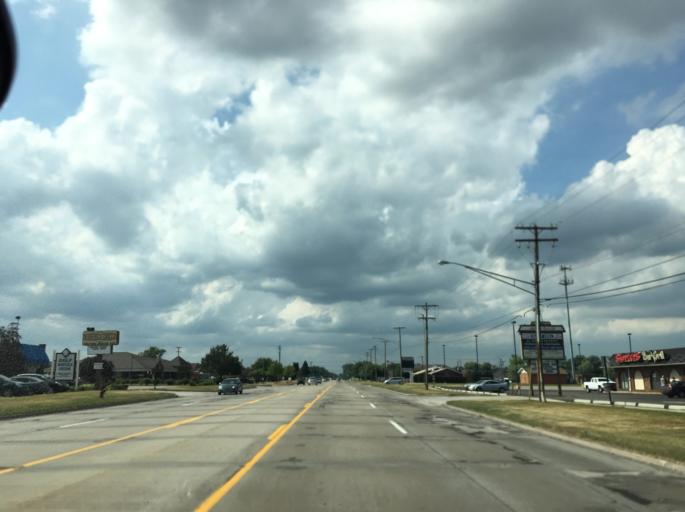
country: US
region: Michigan
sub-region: Macomb County
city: Fraser
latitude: 42.5479
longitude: -82.9579
